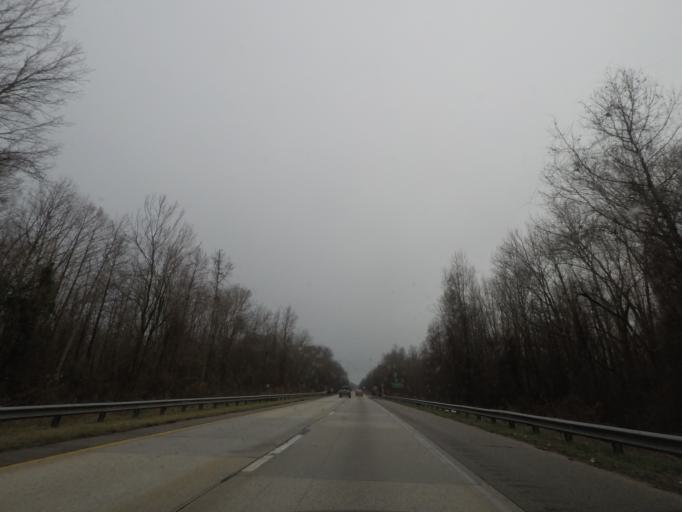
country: US
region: South Carolina
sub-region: Clarendon County
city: Manning
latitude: 33.7338
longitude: -80.2180
